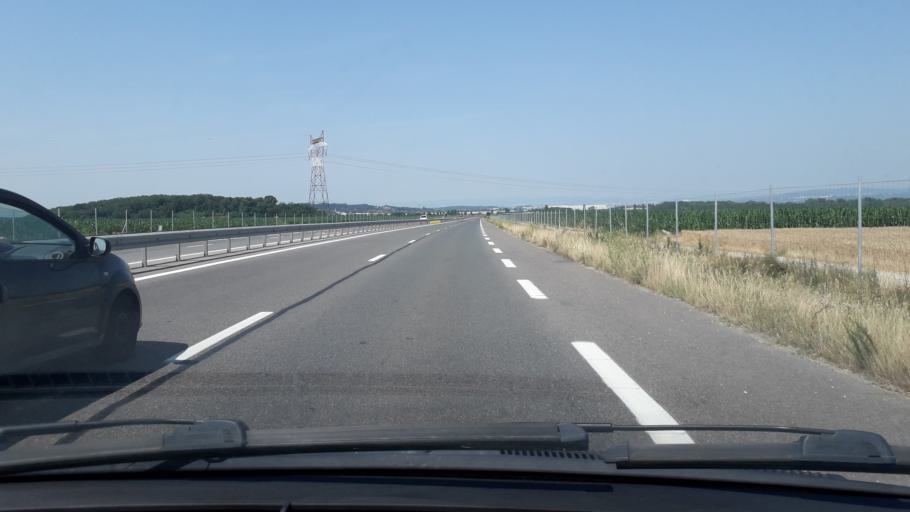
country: FR
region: Rhone-Alpes
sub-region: Departement de l'Isere
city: Janneyrias
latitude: 45.7670
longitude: 5.1145
